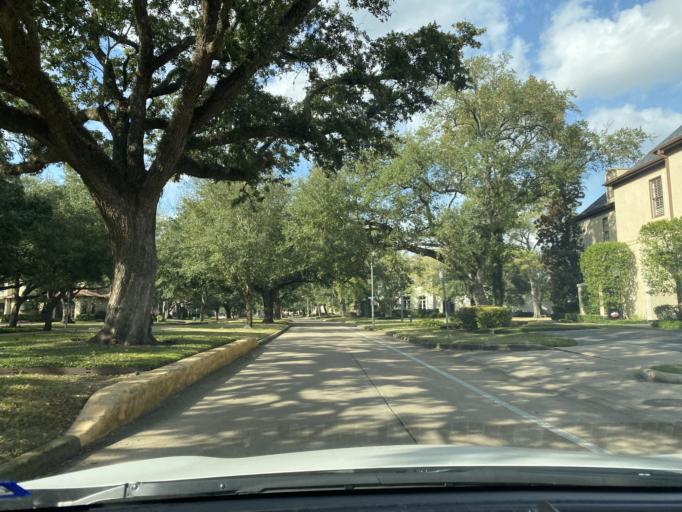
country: US
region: Texas
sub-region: Harris County
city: Hunters Creek Village
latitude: 29.7561
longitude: -95.4714
